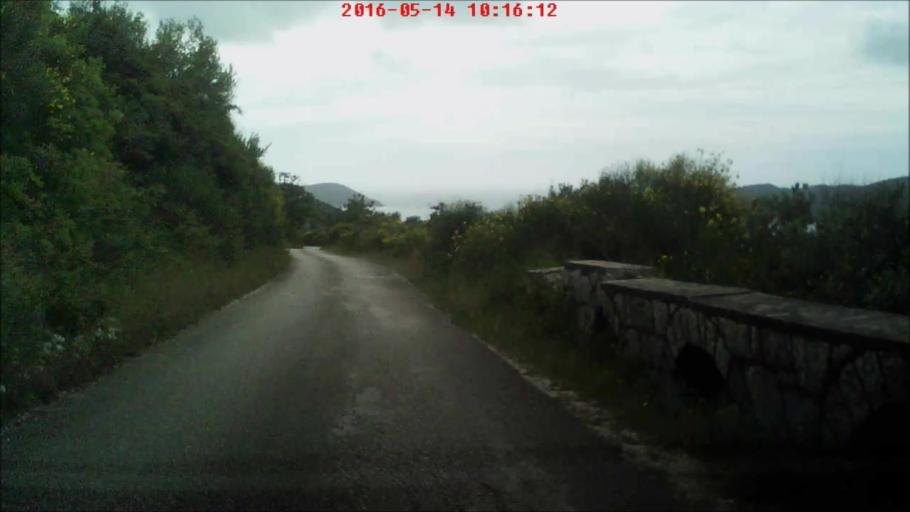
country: HR
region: Dubrovacko-Neretvanska
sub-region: Grad Dubrovnik
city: Mokosica
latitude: 42.7266
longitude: 17.9630
